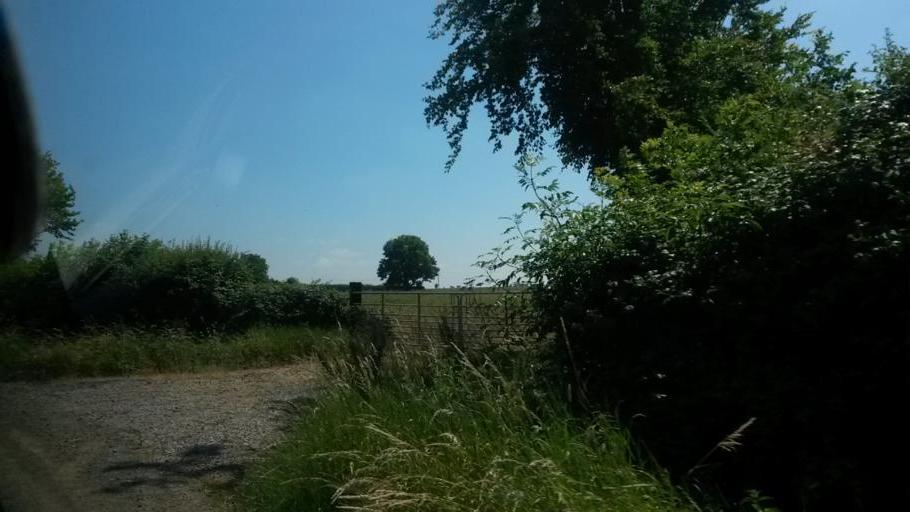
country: IE
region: Leinster
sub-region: Fingal County
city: Swords
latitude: 53.5254
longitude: -6.2956
